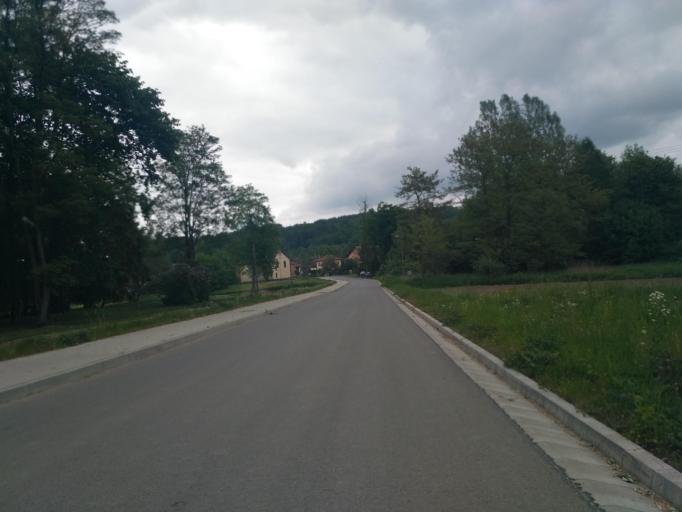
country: PL
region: Subcarpathian Voivodeship
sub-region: Powiat krosnienski
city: Wojaszowka
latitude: 49.7724
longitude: 21.6858
